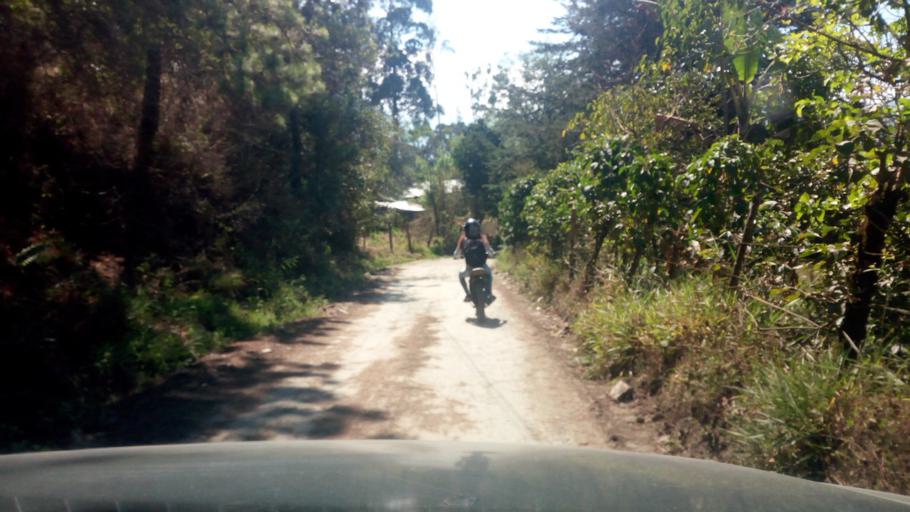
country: CO
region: Boyaca
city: Somondoco
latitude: 4.9868
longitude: -73.4274
